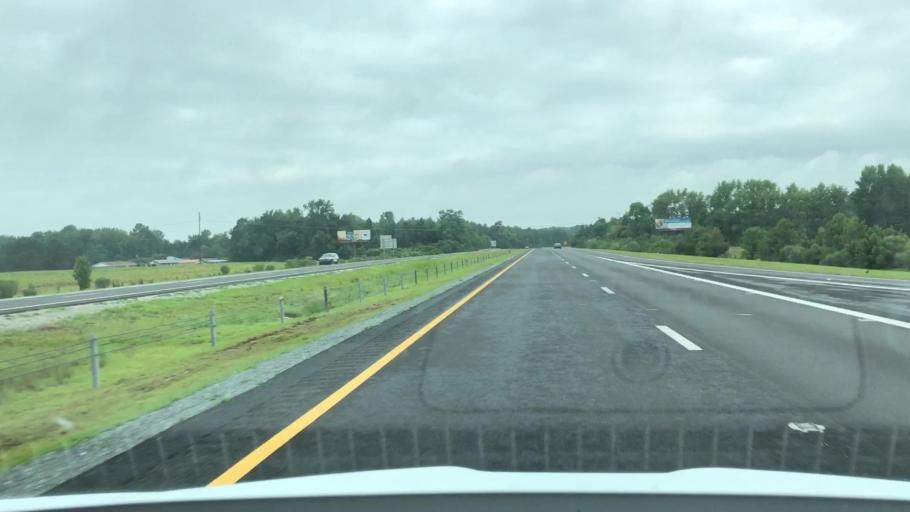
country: US
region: North Carolina
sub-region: Wayne County
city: Fremont
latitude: 35.4978
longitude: -77.9975
